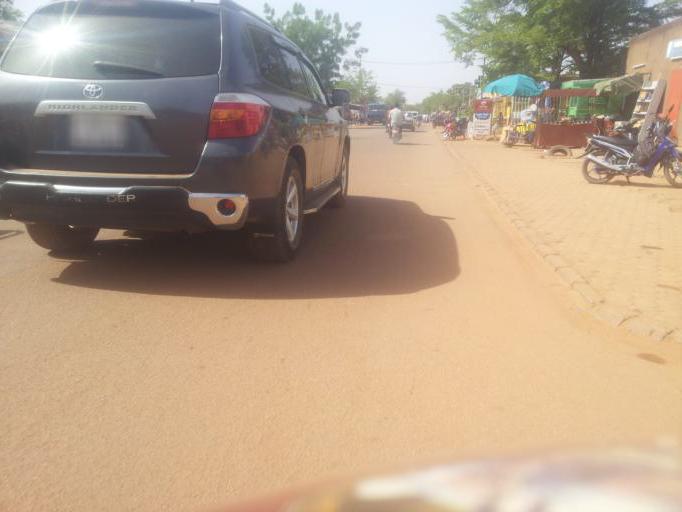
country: BF
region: Centre
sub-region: Kadiogo Province
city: Ouagadougou
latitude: 12.3790
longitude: -1.5399
